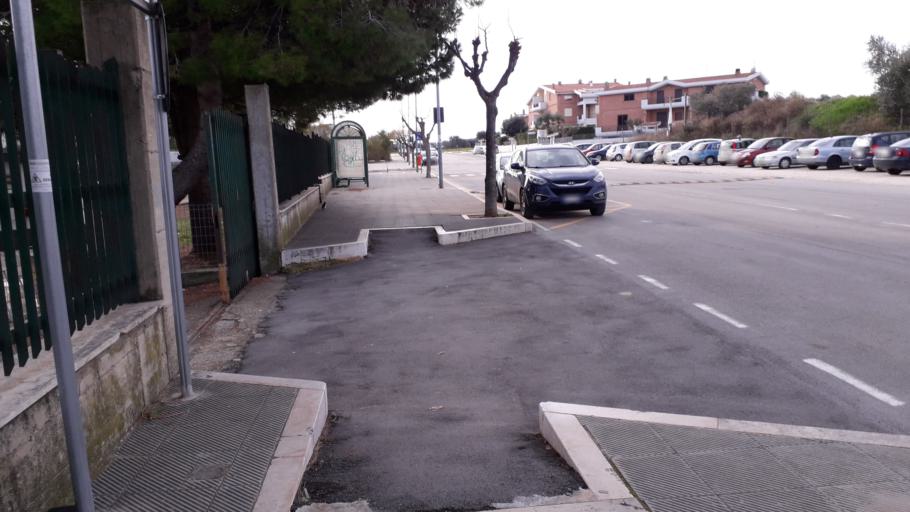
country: IT
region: Molise
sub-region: Provincia di Campobasso
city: Campomarino
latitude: 41.9523
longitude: 15.0318
